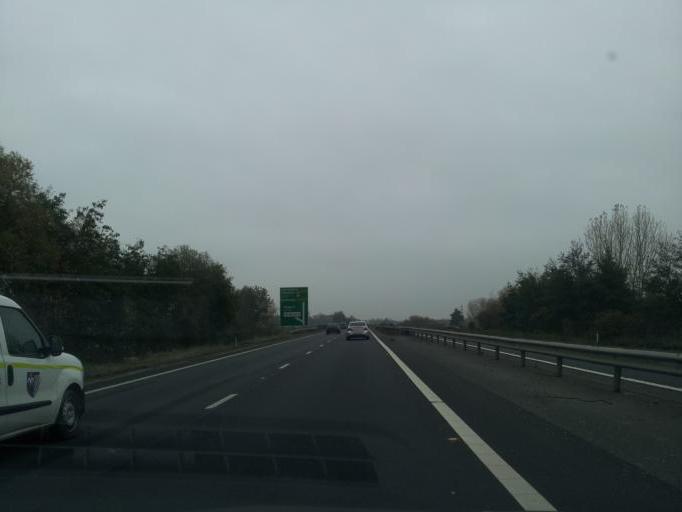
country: GB
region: England
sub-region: Bedford
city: Cople
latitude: 52.1431
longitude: -0.4018
